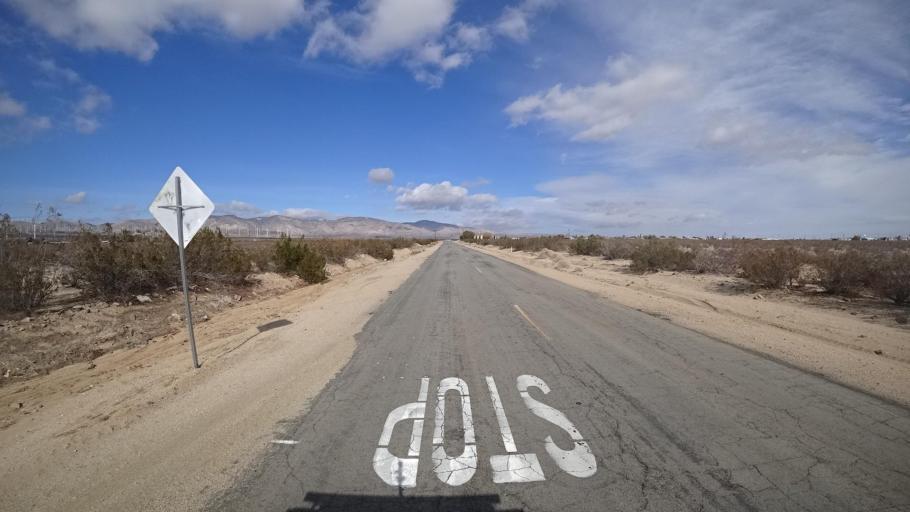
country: US
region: California
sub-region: Kern County
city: Mojave
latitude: 35.0579
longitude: -118.1857
